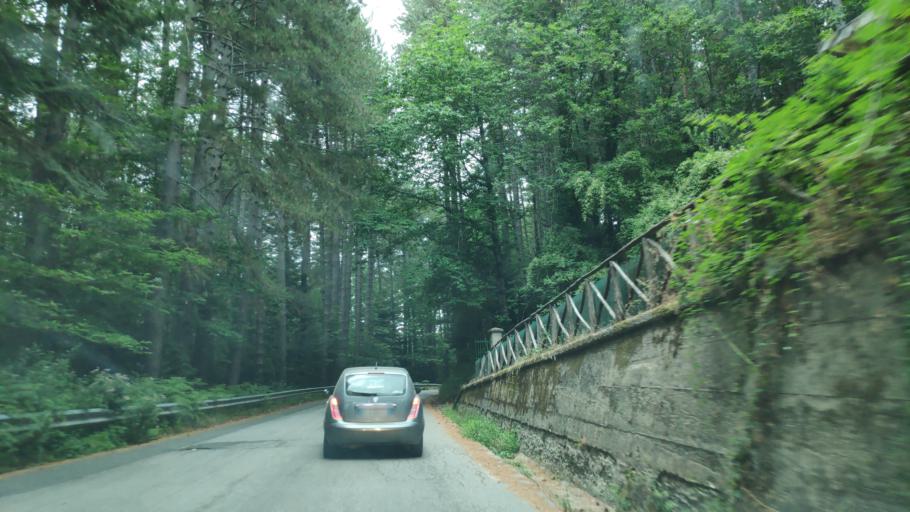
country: IT
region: Calabria
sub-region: Provincia di Vibo-Valentia
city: Mongiana
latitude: 38.5193
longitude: 16.3188
